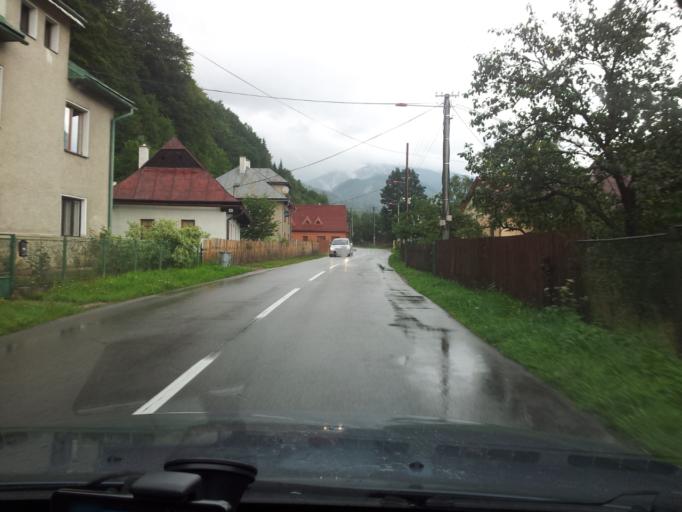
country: SK
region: Banskobystricky
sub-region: Okres Banska Bystrica
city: Brezno
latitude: 48.8551
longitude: 19.6331
